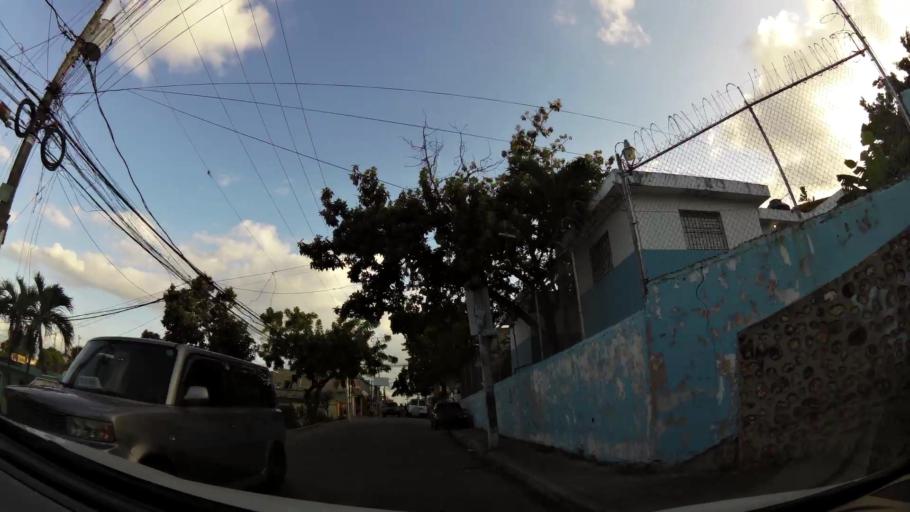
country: DO
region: Nacional
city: La Agustina
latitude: 18.5426
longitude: -69.9263
